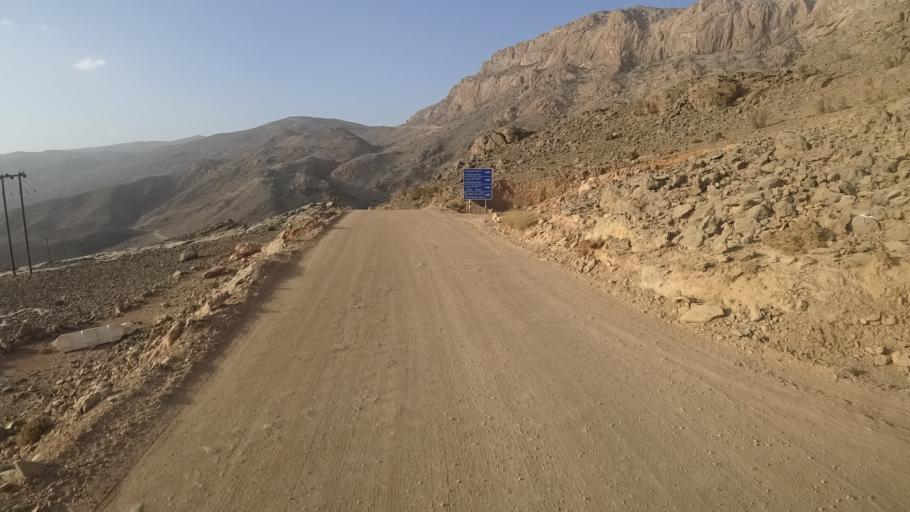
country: OM
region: Al Batinah
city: Rustaq
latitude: 23.2498
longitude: 57.1678
